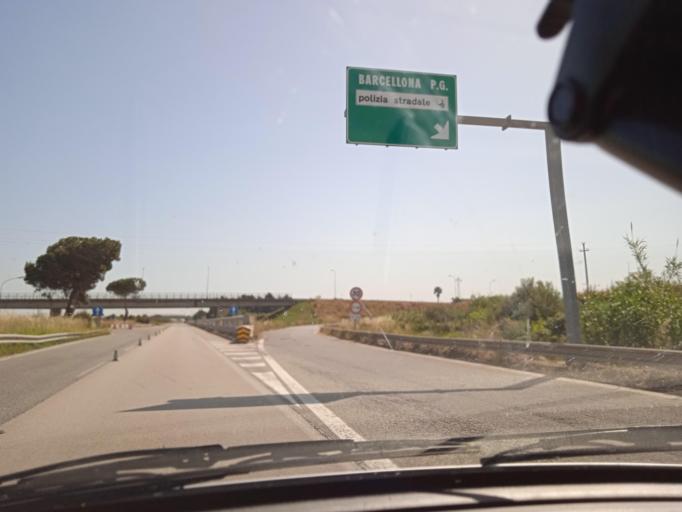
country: IT
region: Sicily
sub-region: Messina
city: Barcellona Pozzo di Gotto
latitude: 38.1550
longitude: 15.1862
